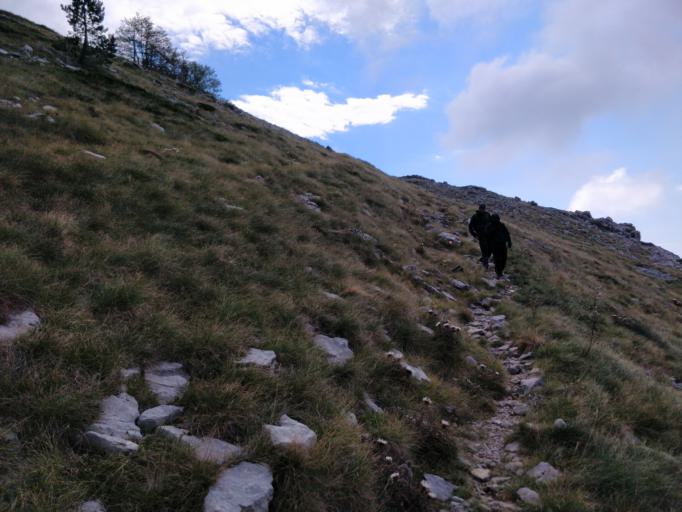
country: HR
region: Zadarska
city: Starigrad
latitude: 44.3793
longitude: 15.4760
